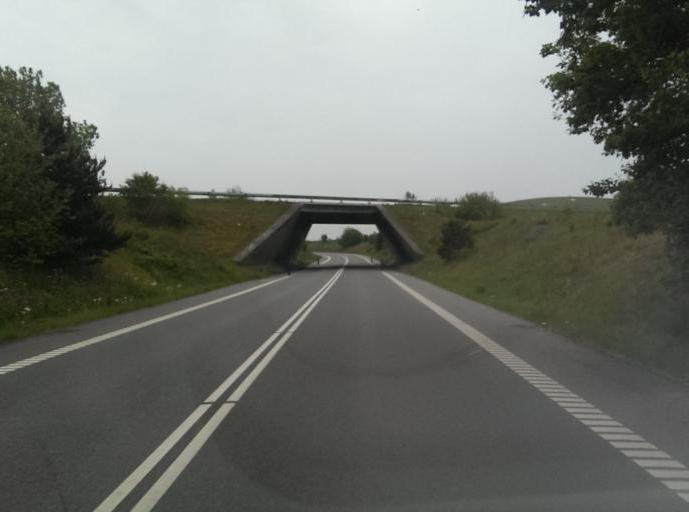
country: DK
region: South Denmark
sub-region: Esbjerg Kommune
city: Esbjerg
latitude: 55.5169
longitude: 8.4886
